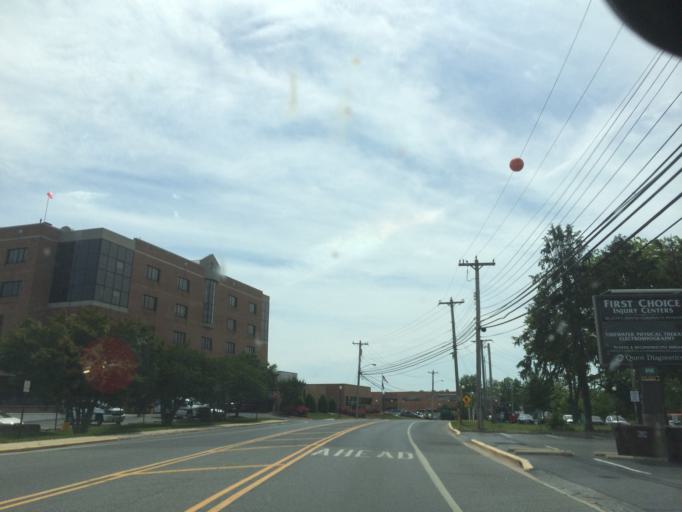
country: US
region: Delaware
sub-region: Sussex County
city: Seaford
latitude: 38.6428
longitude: -75.6034
